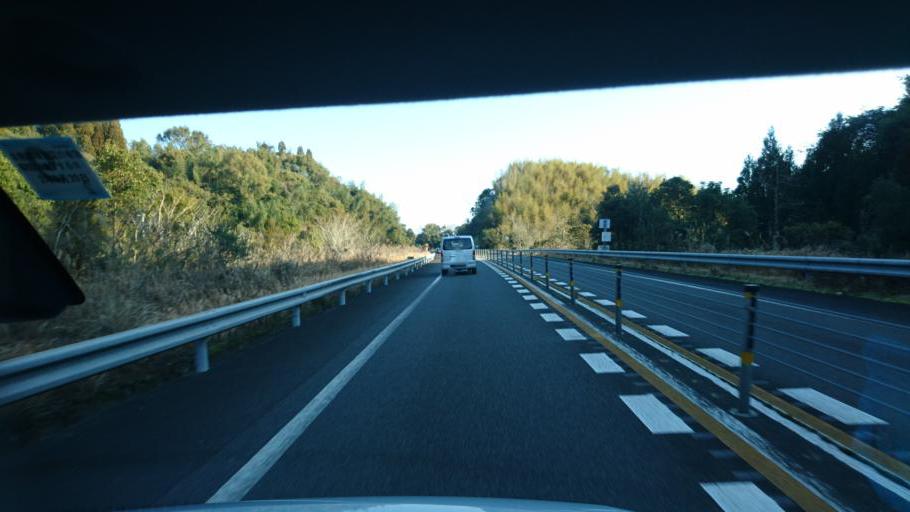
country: JP
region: Miyazaki
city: Tsuma
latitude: 32.0232
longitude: 131.3909
